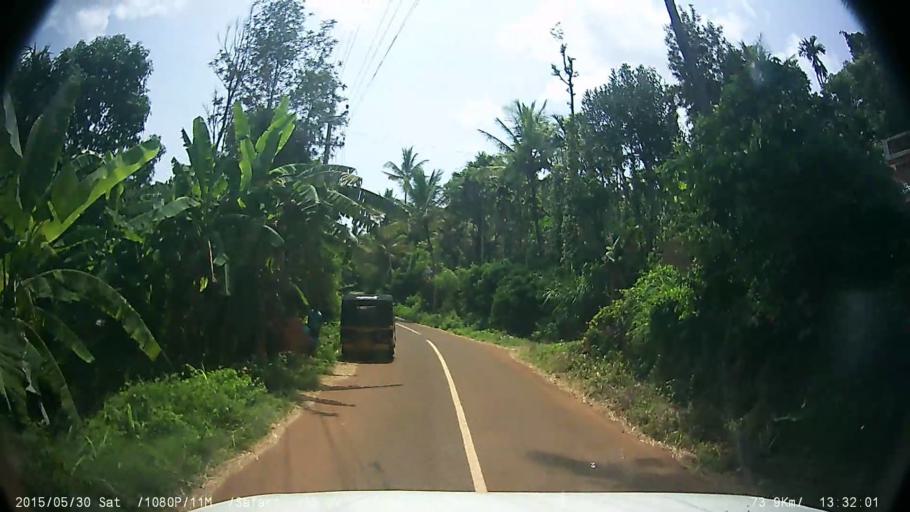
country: IN
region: Kerala
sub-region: Wayanad
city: Panamaram
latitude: 11.8174
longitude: 76.0806
